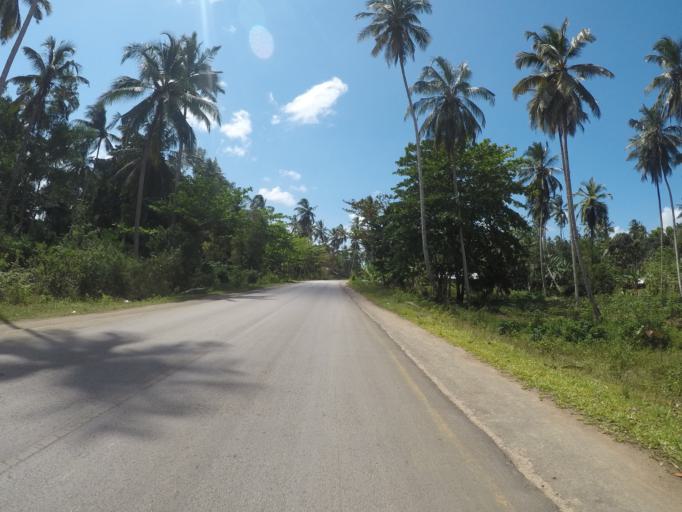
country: TZ
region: Zanzibar Central/South
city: Koani
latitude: -6.1425
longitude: 39.3272
